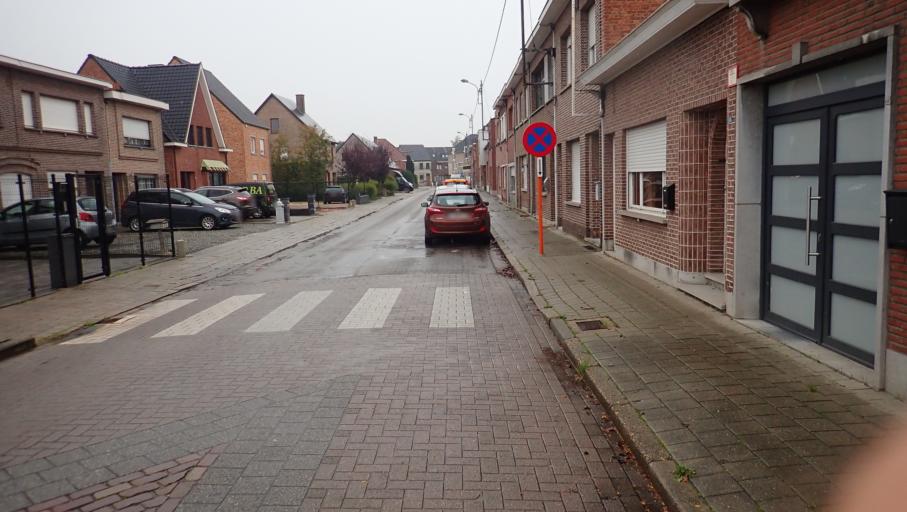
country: BE
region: Flanders
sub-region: Provincie Antwerpen
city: Berlaar
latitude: 51.1158
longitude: 4.6426
